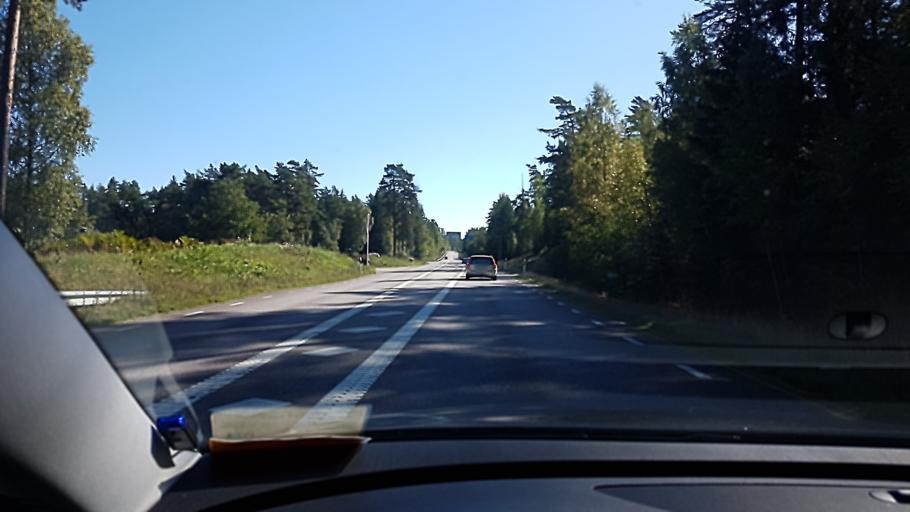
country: SE
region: Kronoberg
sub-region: Lessebo Kommun
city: Lessebo
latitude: 56.7819
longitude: 15.2286
